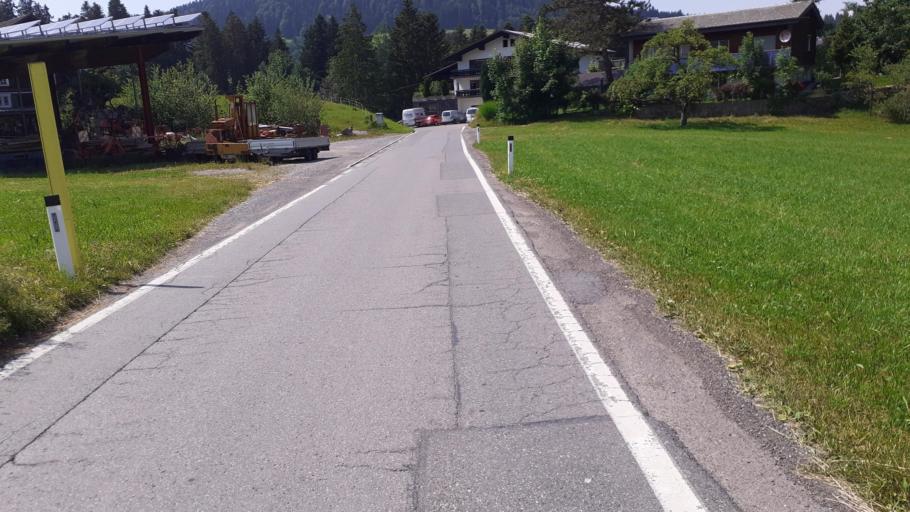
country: AT
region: Vorarlberg
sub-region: Politischer Bezirk Bregenz
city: Doren
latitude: 47.4600
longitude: 9.8355
